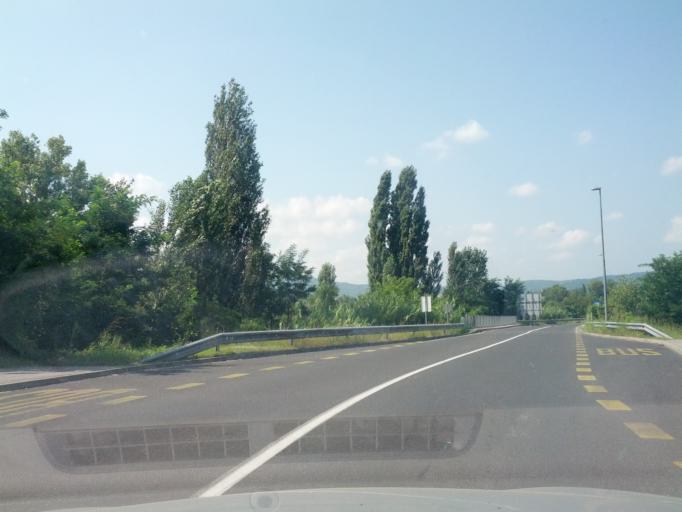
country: SI
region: Koper-Capodistria
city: Spodnje Skofije
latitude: 45.5576
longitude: 13.7860
